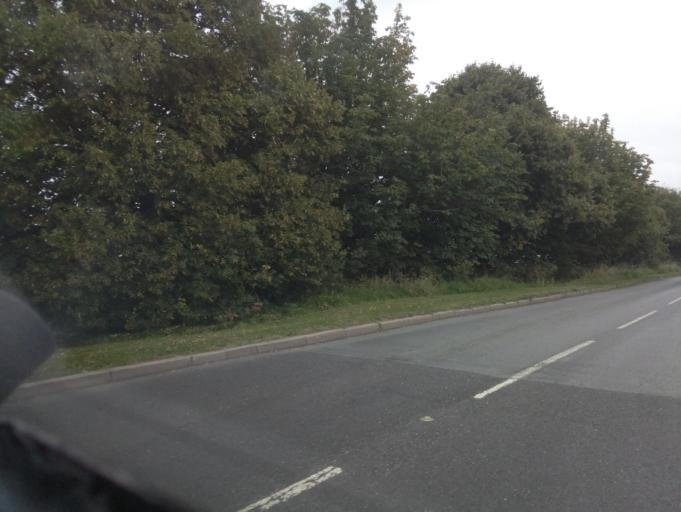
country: GB
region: England
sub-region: Derbyshire
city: Bradley
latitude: 53.0196
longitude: -1.6145
